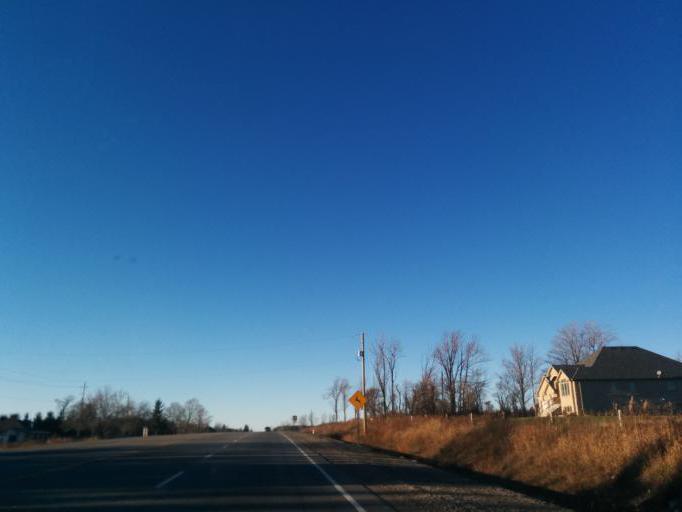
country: CA
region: Ontario
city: Orangeville
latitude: 43.8690
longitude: -80.0075
